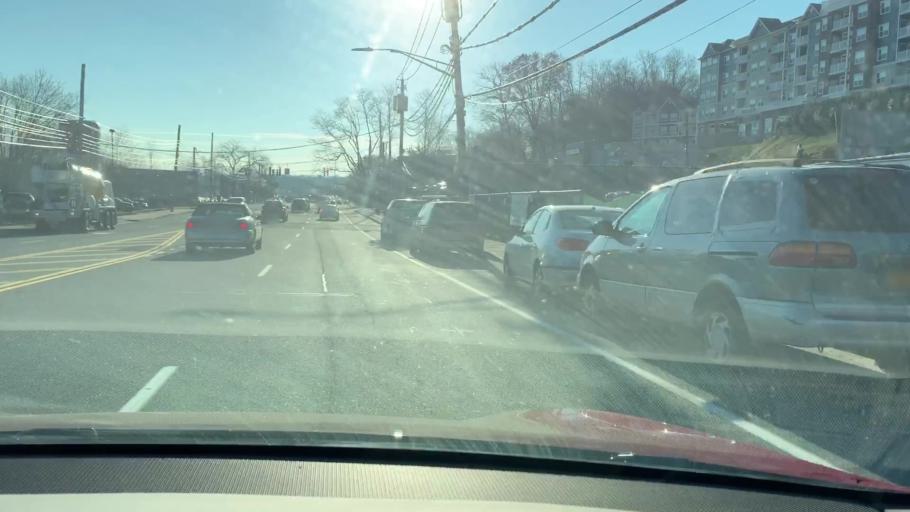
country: US
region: New York
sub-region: Westchester County
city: Fairview
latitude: 41.0484
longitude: -73.8086
